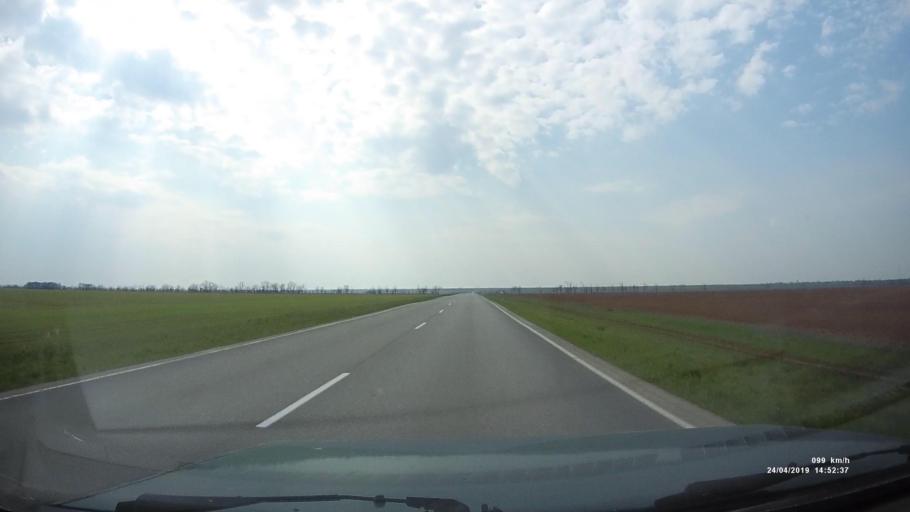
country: RU
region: Rostov
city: Remontnoye
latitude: 46.5305
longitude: 43.6767
